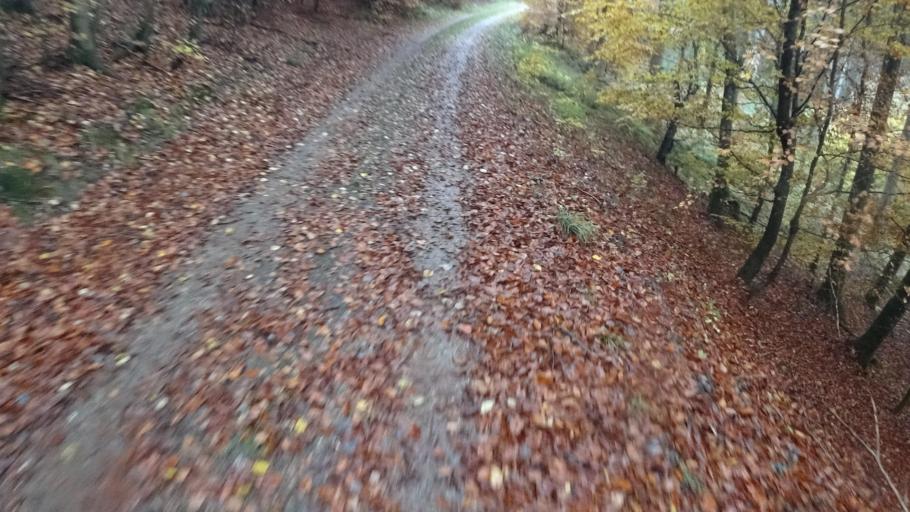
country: DE
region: Rheinland-Pfalz
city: Utzenhain
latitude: 50.1517
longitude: 7.6505
